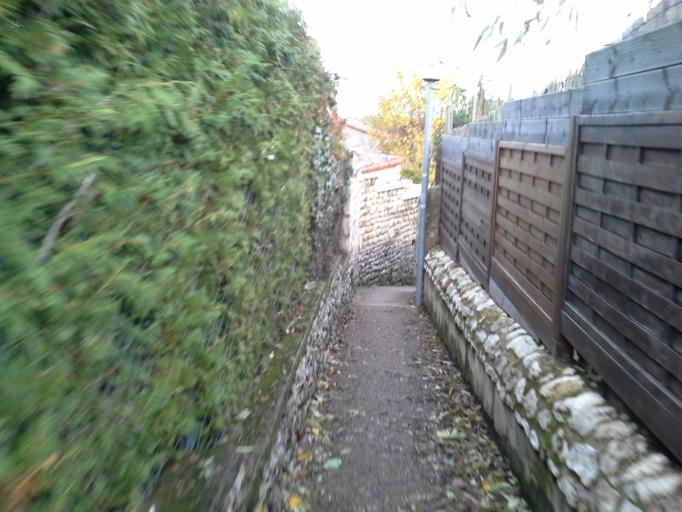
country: FR
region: Poitou-Charentes
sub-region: Departement de la Vienne
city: Chauvigny
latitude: 46.5720
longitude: 0.6486
